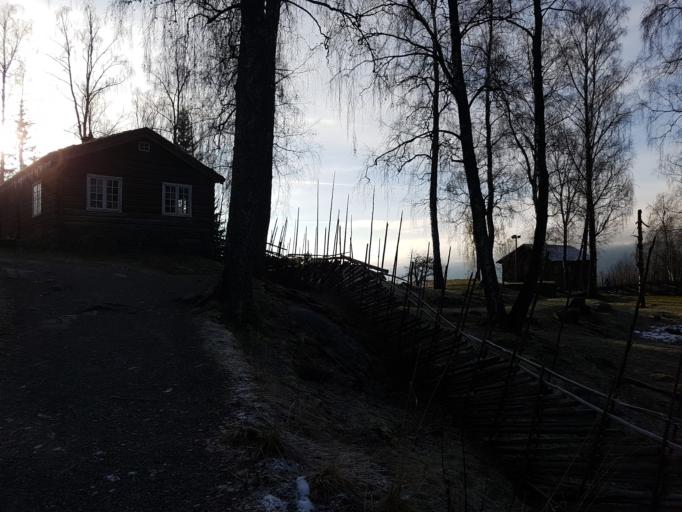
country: NO
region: Oppland
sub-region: Lillehammer
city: Lillehammer
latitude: 61.1101
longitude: 10.4768
